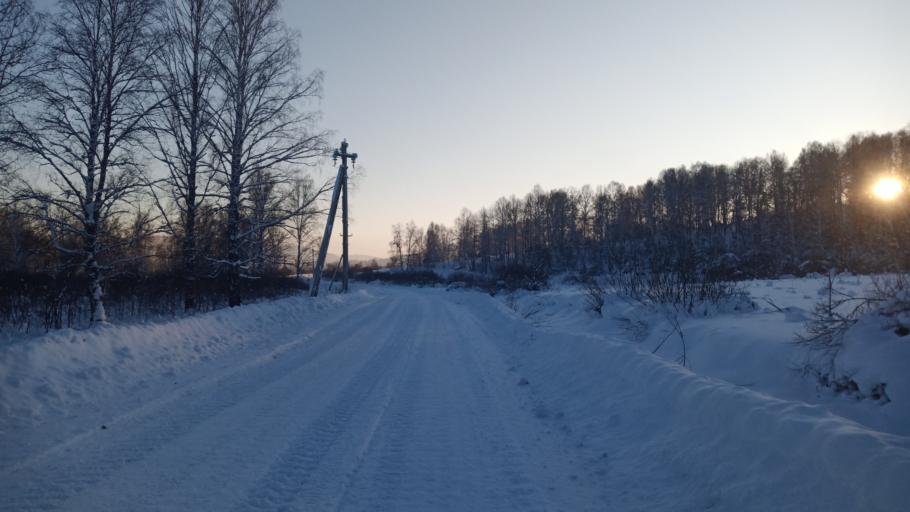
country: RU
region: Altai Krai
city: Krasnogorskoye
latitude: 52.1258
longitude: 86.2045
